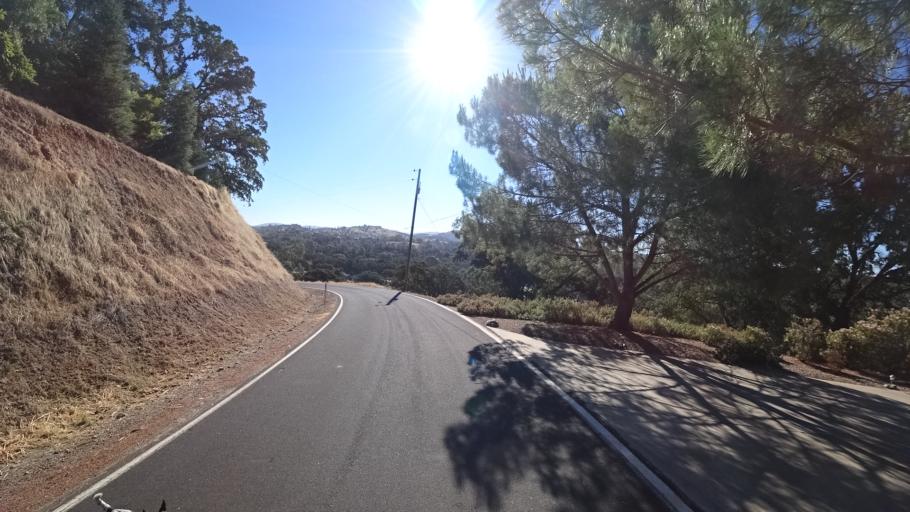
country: US
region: California
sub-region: Calaveras County
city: Rancho Calaveras
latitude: 38.1168
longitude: -120.8664
